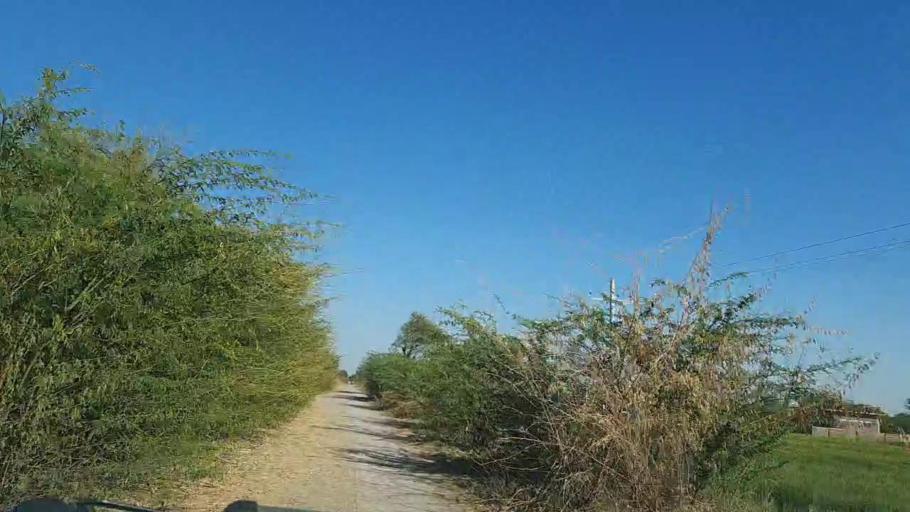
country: PK
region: Sindh
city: Dhoro Naro
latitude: 25.5155
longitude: 69.4859
